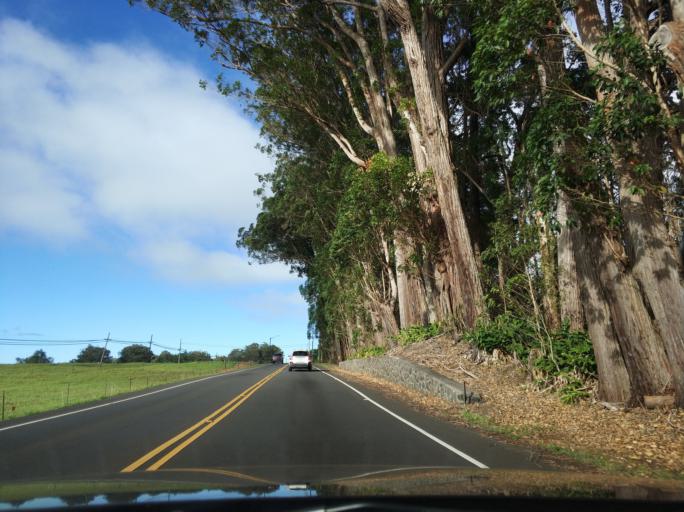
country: US
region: Hawaii
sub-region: Hawaii County
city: Waimea
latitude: 20.0415
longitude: -155.6037
